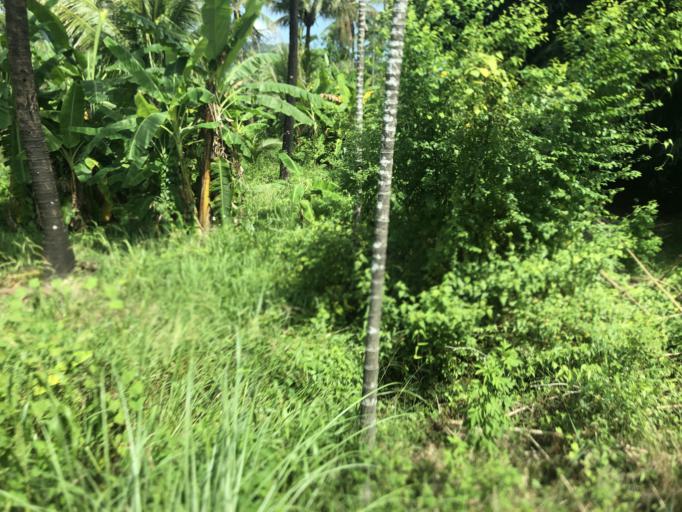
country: TW
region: Taiwan
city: Yujing
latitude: 22.9137
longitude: 120.5688
